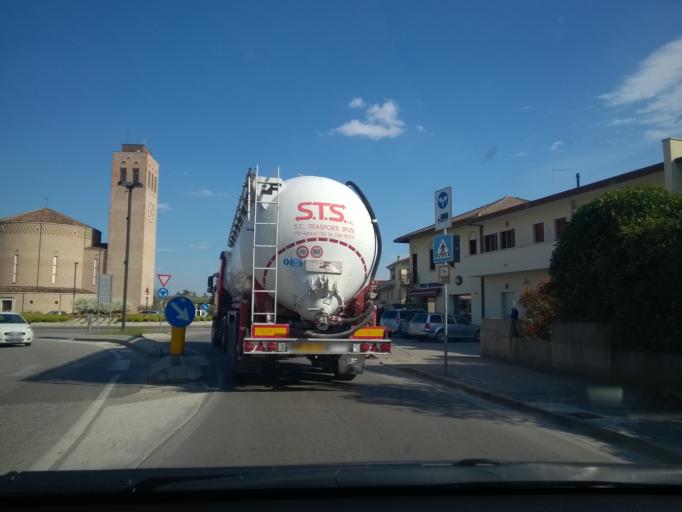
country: IT
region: Veneto
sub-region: Provincia di Treviso
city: Priula-Colfosco
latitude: 45.8227
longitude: 12.2534
